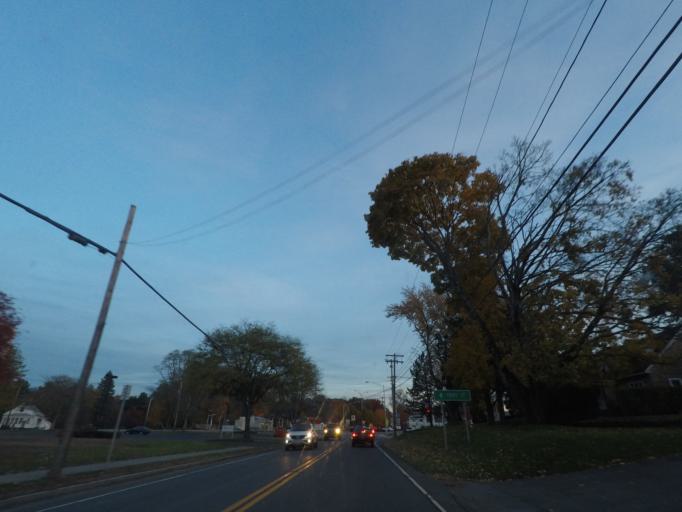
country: US
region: New York
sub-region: Schenectady County
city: Rotterdam
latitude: 42.7659
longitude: -73.9399
